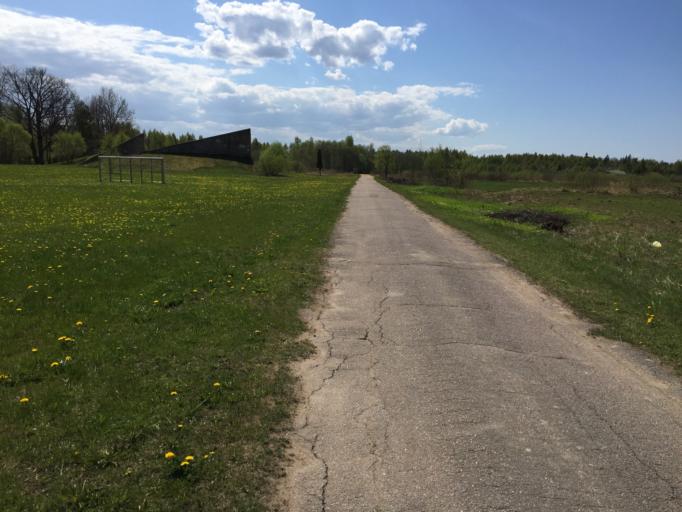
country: LV
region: Saulkrastu
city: Saulkrasti
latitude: 57.3263
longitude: 24.4882
